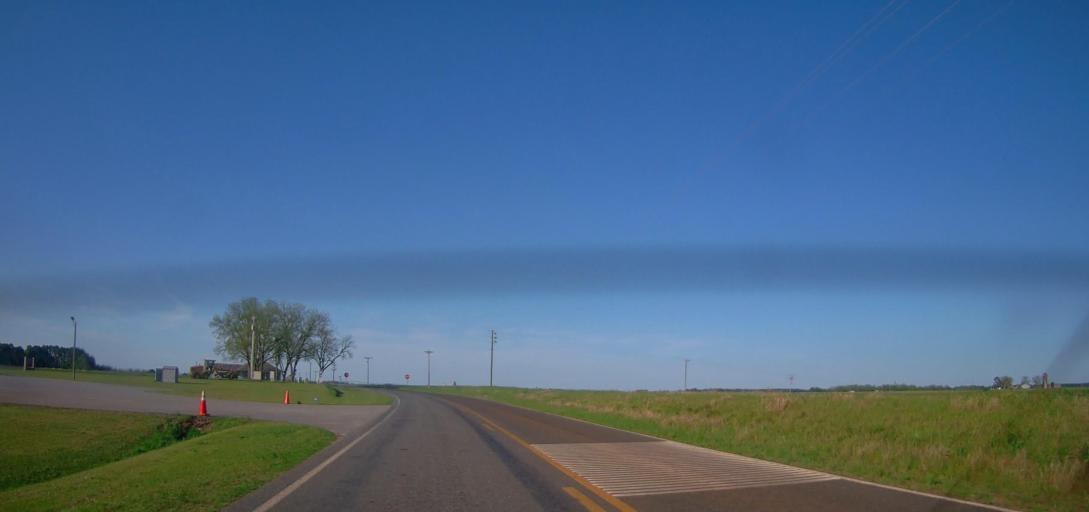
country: US
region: Georgia
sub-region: Macon County
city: Marshallville
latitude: 32.3570
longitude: -83.9402
